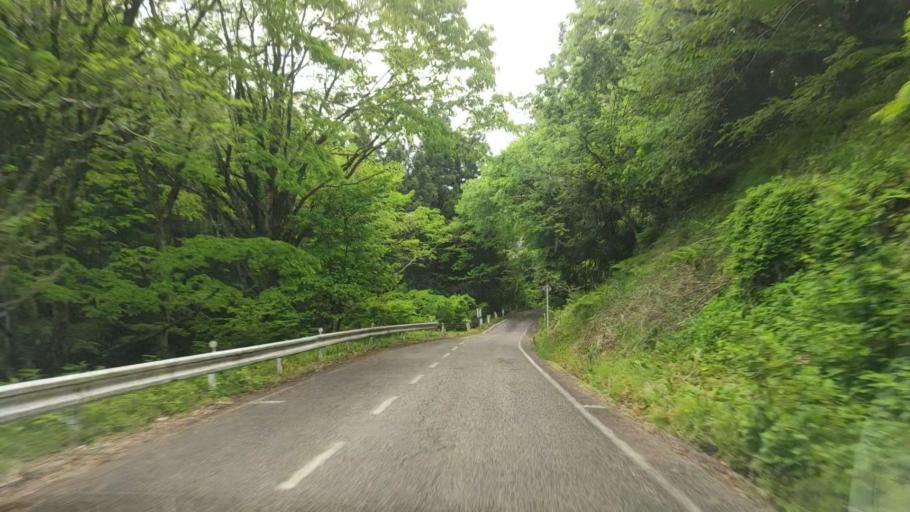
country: JP
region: Niigata
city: Kamo
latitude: 37.7165
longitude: 139.0885
